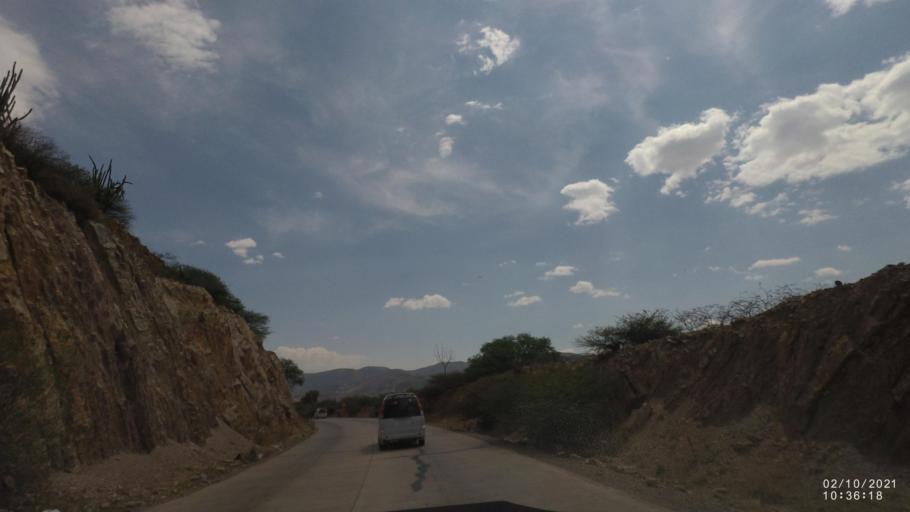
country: BO
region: Cochabamba
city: Capinota
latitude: -17.6521
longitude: -66.2586
